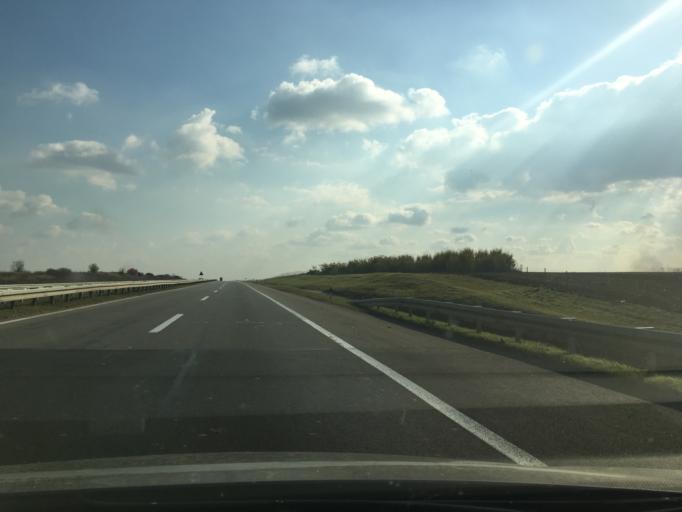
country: RS
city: Beska
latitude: 45.1184
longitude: 20.0973
